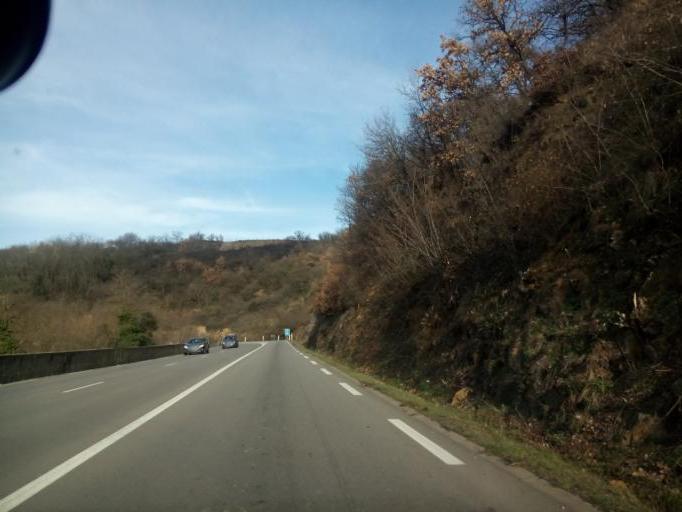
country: FR
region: Rhone-Alpes
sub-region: Departement de l'Ardeche
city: Serrieres
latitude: 45.3109
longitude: 4.7620
